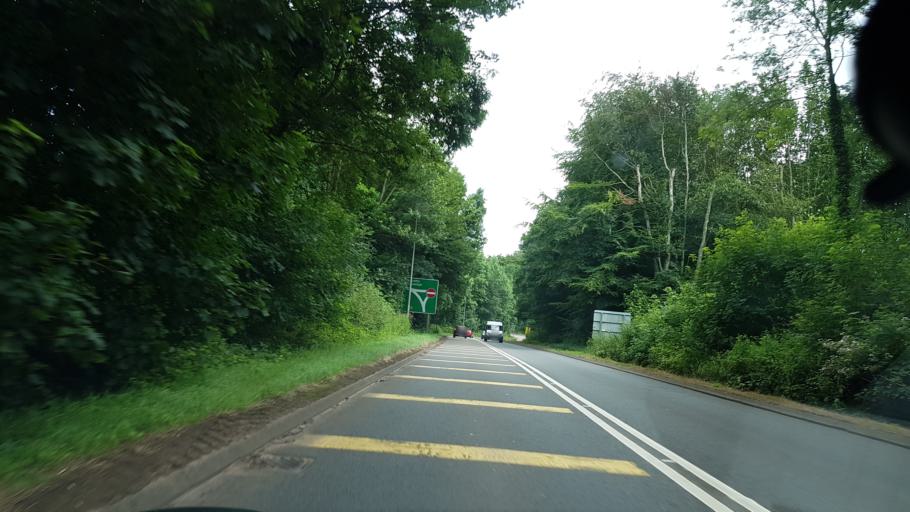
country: GB
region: Wales
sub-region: Monmouthshire
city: Abergavenny
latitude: 51.8113
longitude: -3.0075
